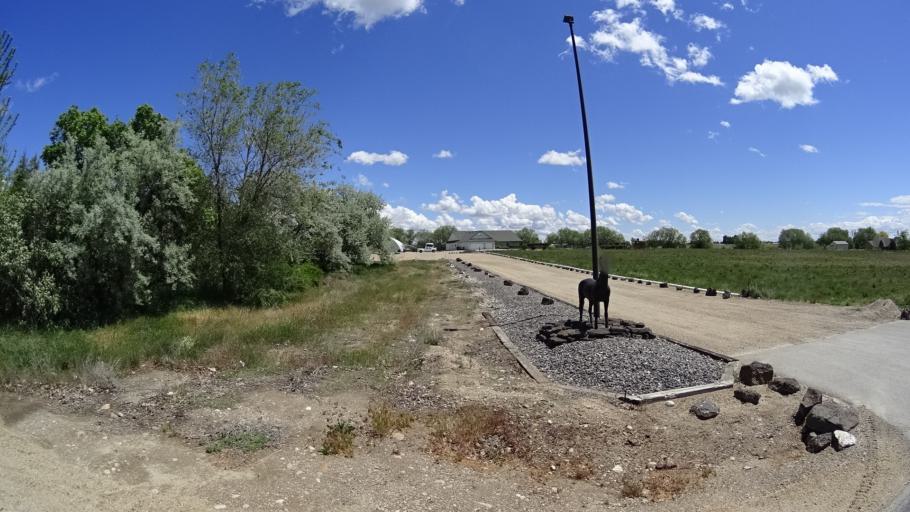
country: US
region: Idaho
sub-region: Ada County
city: Kuna
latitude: 43.5678
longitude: -116.4736
